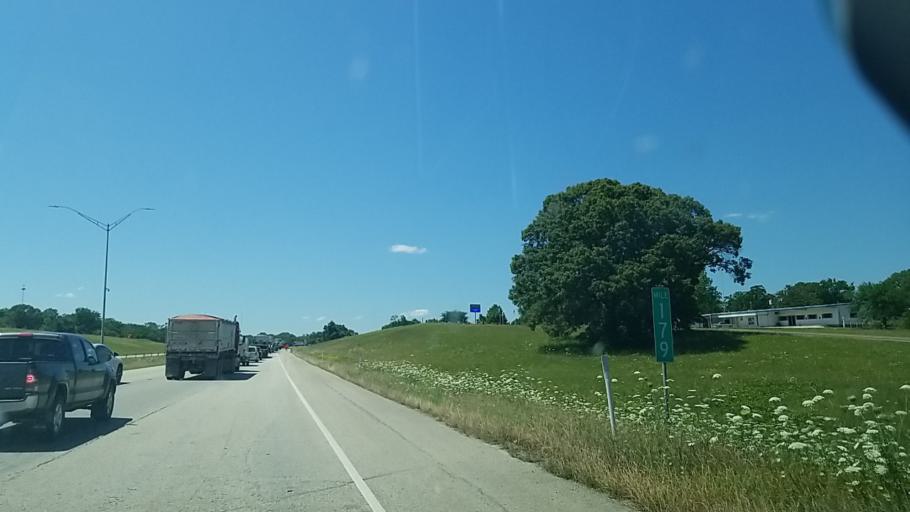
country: US
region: Texas
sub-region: Leon County
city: Buffalo
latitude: 31.4549
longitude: -96.0793
